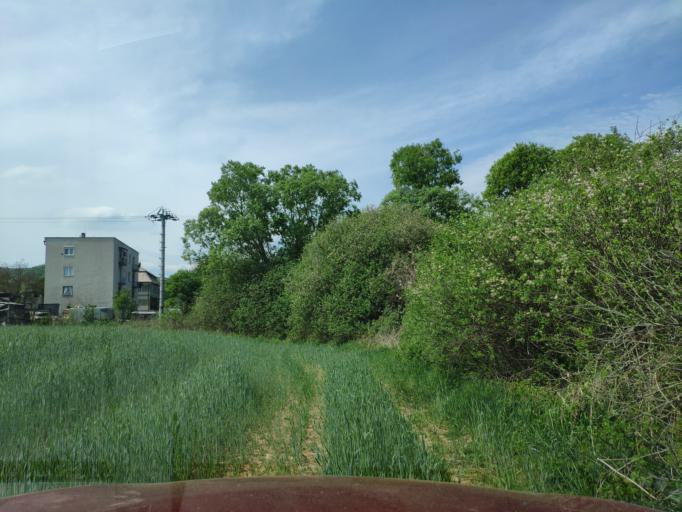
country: SK
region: Banskobystricky
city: Rimavska Sobota
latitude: 48.4794
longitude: 20.0747
